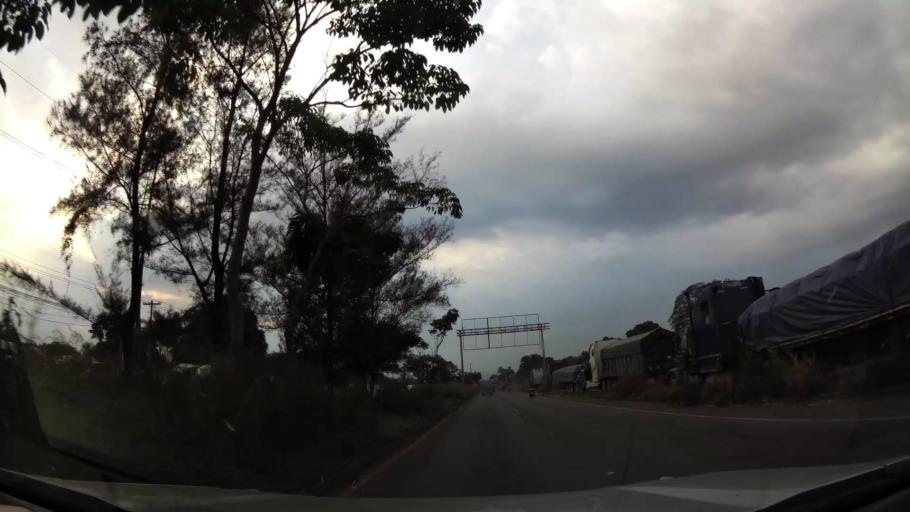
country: GT
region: Escuintla
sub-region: Municipio de Escuintla
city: Escuintla
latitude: 14.2814
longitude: -90.7846
